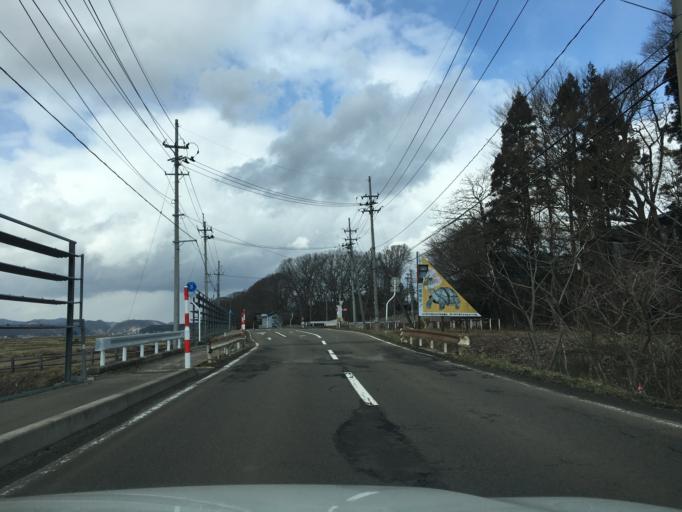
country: JP
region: Akita
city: Takanosu
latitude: 40.1427
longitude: 140.3484
